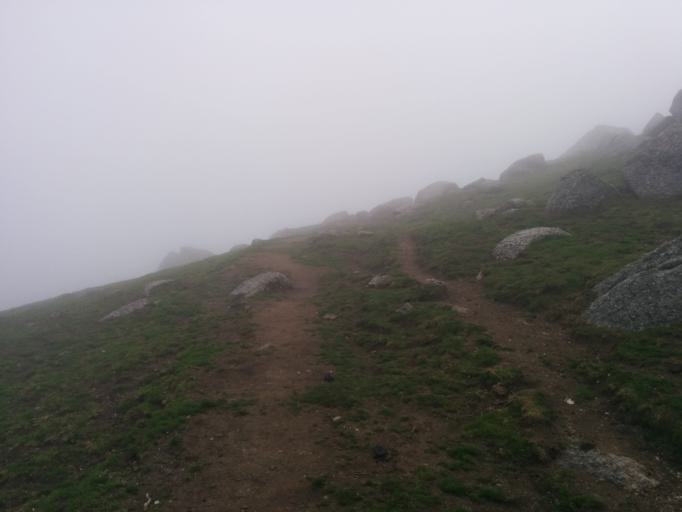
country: IN
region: Himachal Pradesh
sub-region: Kangra
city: Dharmsala
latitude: 32.2719
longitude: 76.3606
